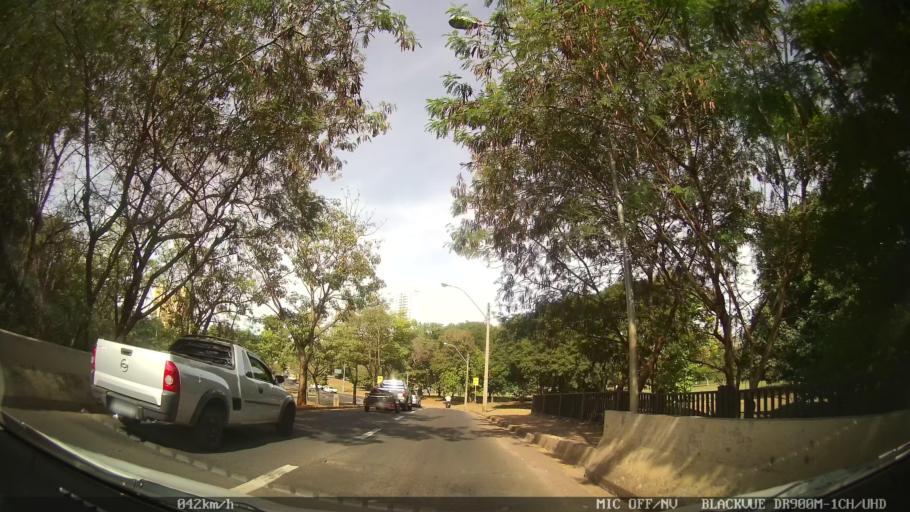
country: BR
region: Sao Paulo
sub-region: Piracicaba
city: Piracicaba
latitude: -22.7258
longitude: -47.6664
